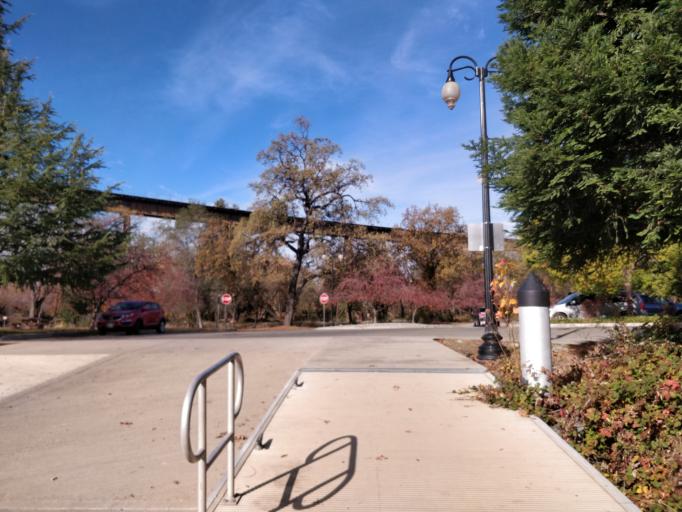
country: US
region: California
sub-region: Shasta County
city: Redding
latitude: 40.5940
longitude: -122.3983
